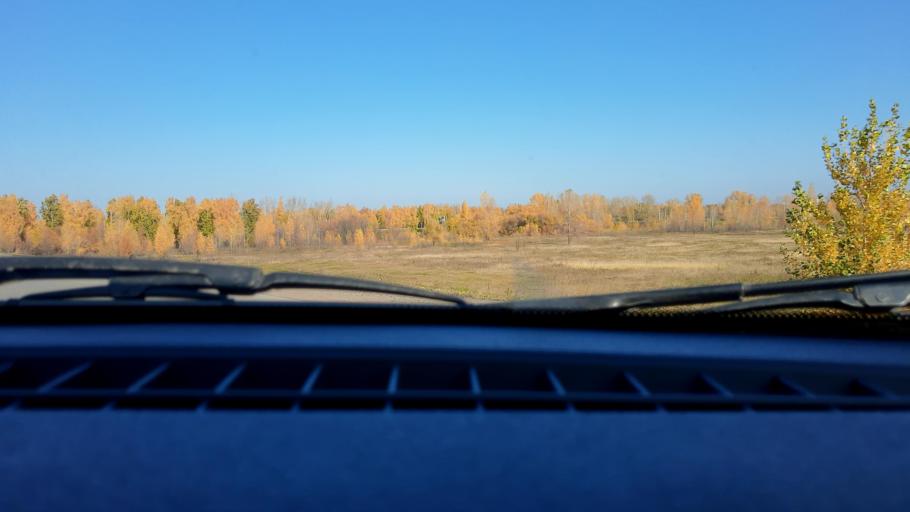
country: RU
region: Bashkortostan
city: Mikhaylovka
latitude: 54.7659
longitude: 55.9146
